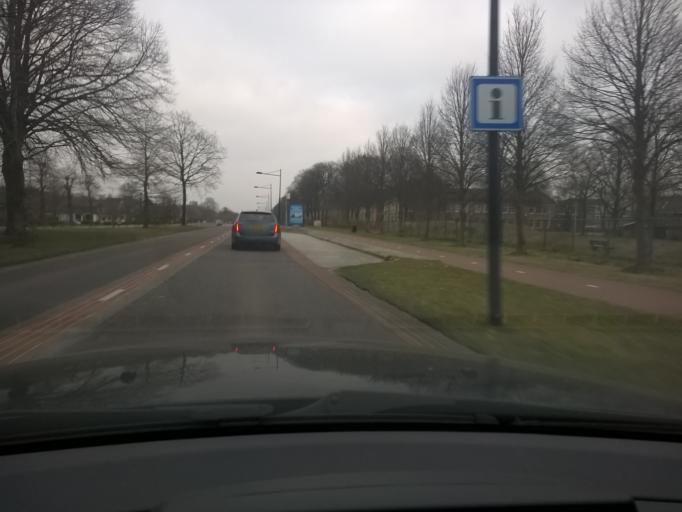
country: NL
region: Drenthe
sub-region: Gemeente Assen
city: Assen
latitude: 52.9943
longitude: 6.5373
